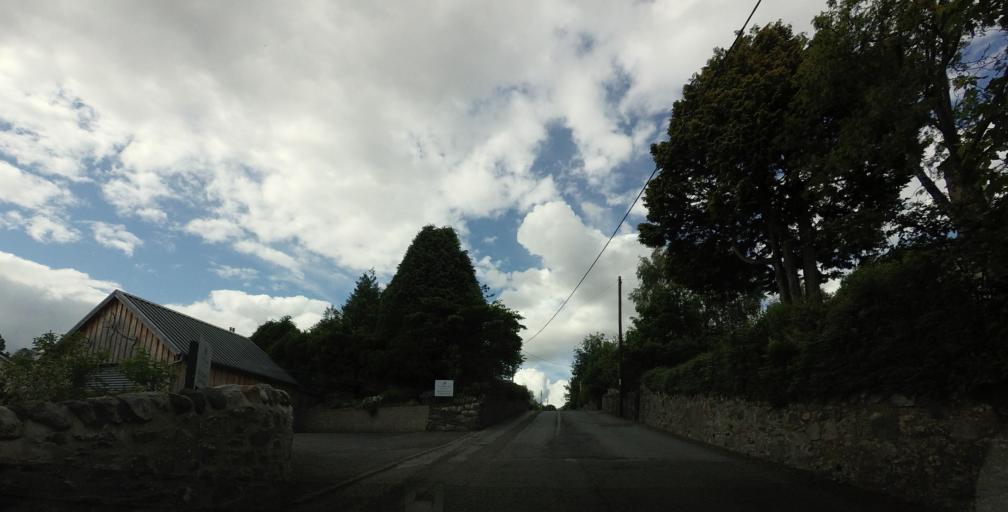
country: GB
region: Scotland
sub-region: Perth and Kinross
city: Pitlochry
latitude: 56.7022
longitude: -3.7242
